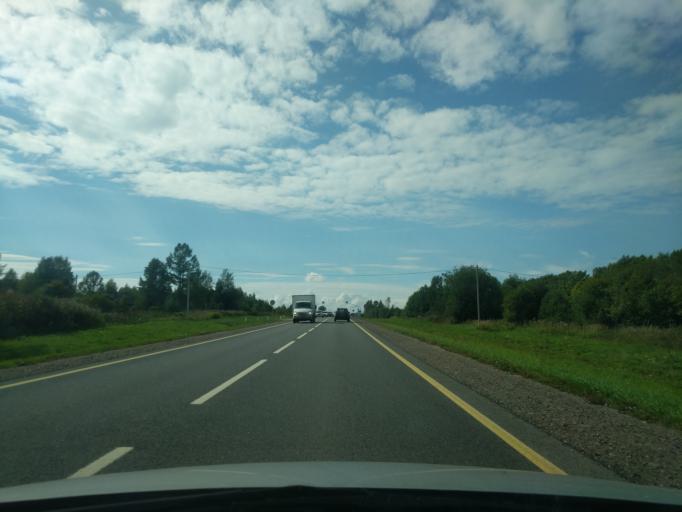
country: RU
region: Kostroma
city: Oktyabr'skiy
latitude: 57.7980
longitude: 41.2290
